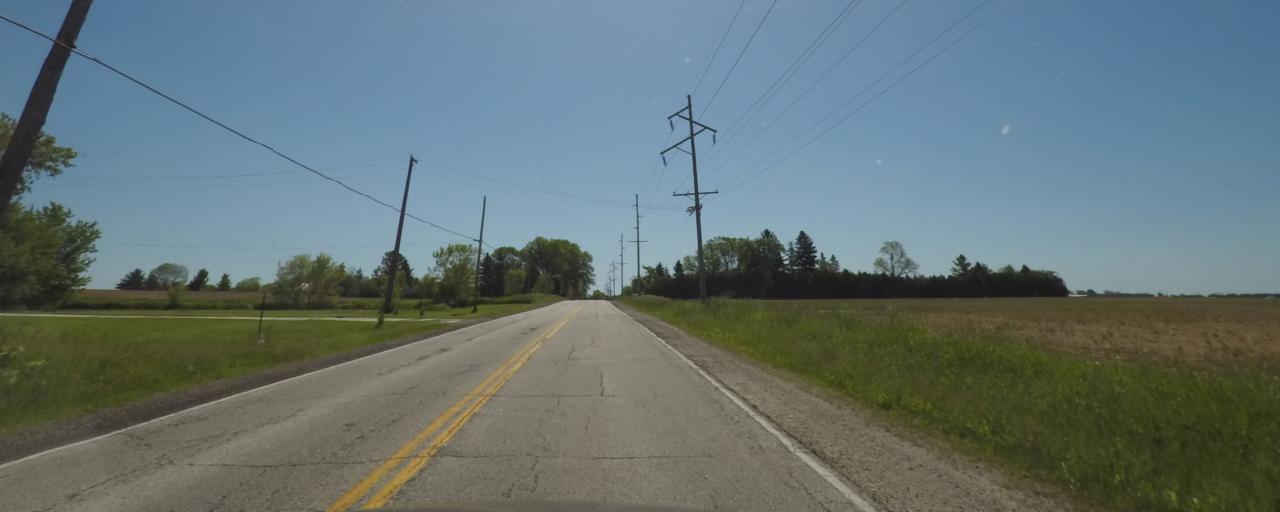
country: US
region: Wisconsin
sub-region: Sheboygan County
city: Sheboygan Falls
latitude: 43.7415
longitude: -87.8595
